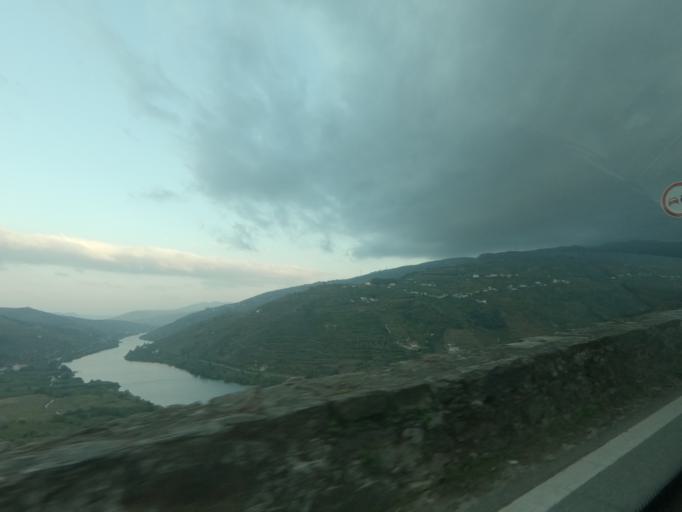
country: PT
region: Vila Real
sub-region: Mesao Frio
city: Mesao Frio
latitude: 41.1602
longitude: -7.8787
